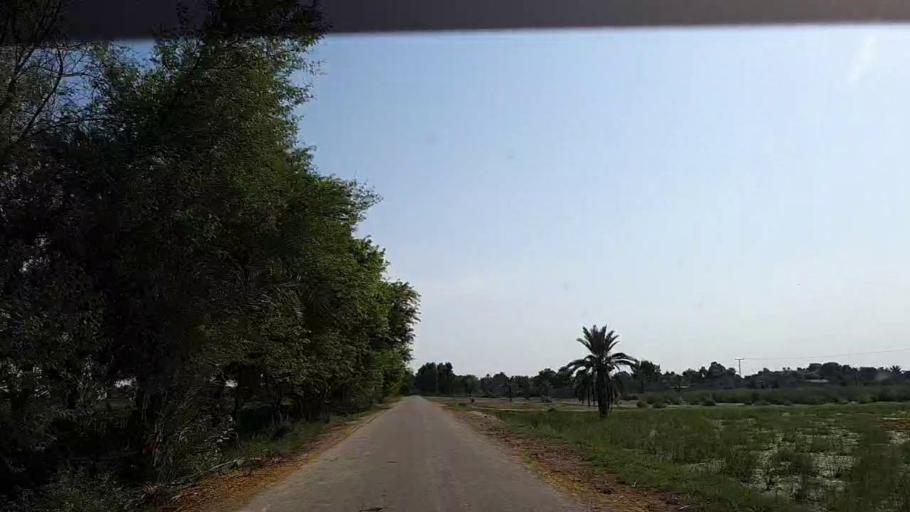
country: PK
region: Sindh
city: Adilpur
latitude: 27.9248
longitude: 69.2495
